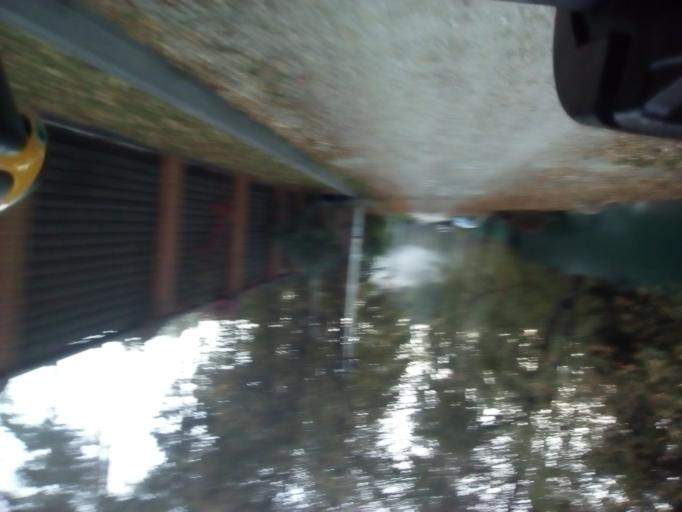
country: RU
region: Moskovskaya
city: Kratovo
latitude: 55.6030
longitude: 38.1781
